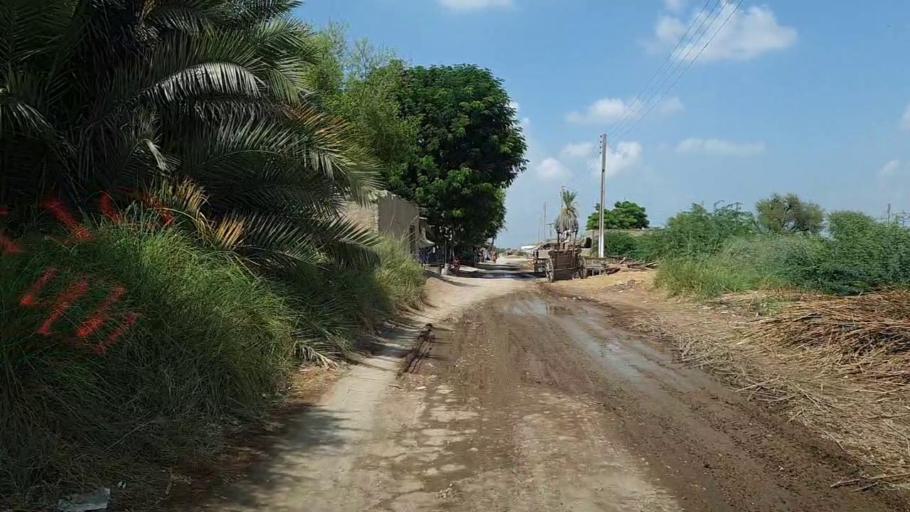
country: PK
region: Sindh
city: Kandiaro
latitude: 27.0269
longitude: 68.2755
